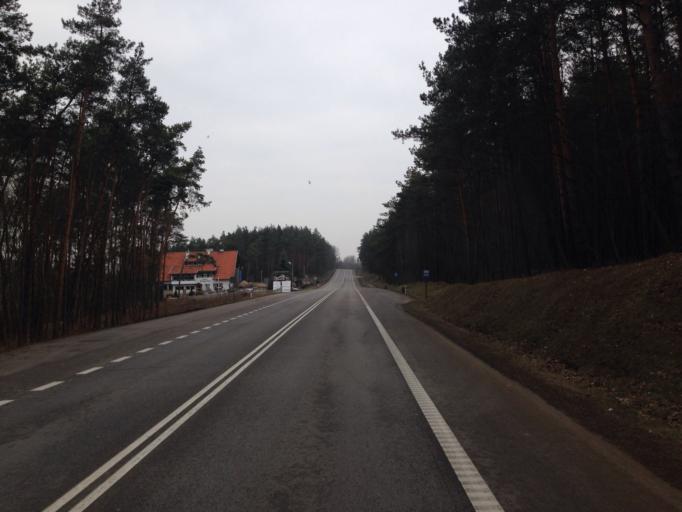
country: PL
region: Pomeranian Voivodeship
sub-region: Powiat starogardzki
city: Smetowo Graniczne
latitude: 53.7559
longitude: 18.7618
